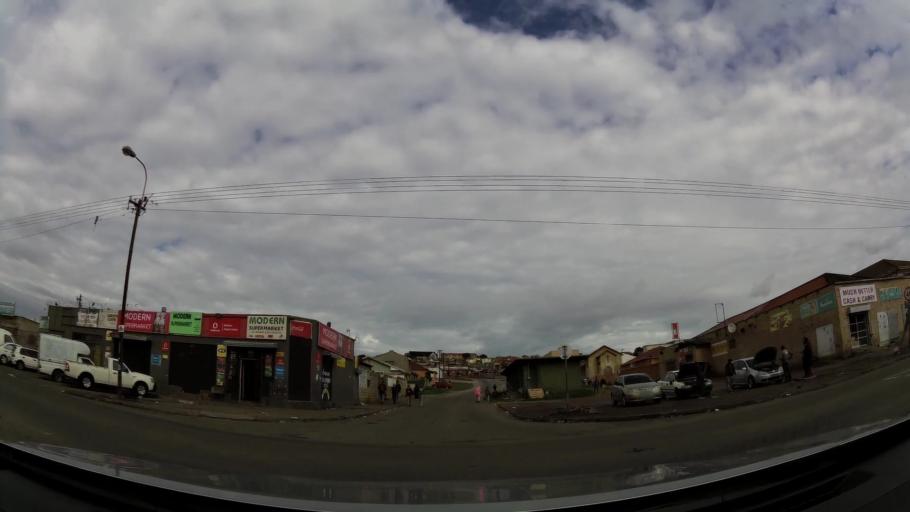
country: ZA
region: Eastern Cape
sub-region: Nelson Mandela Bay Metropolitan Municipality
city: Port Elizabeth
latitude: -33.9317
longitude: 25.5766
